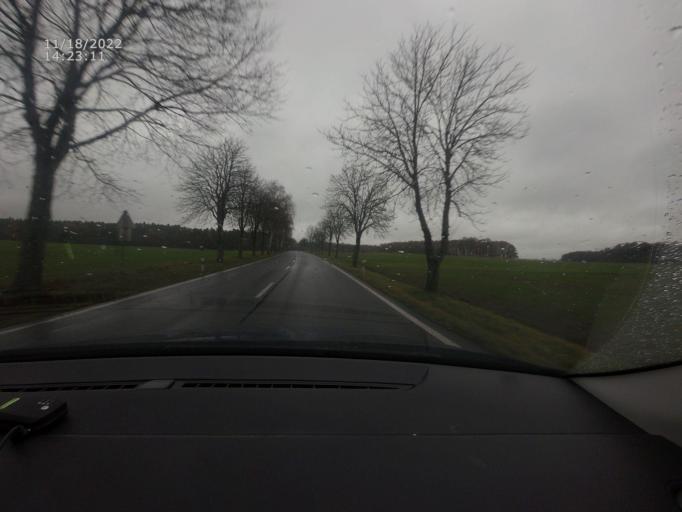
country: CZ
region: Jihocesky
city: Cimelice
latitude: 49.4398
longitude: 14.1033
